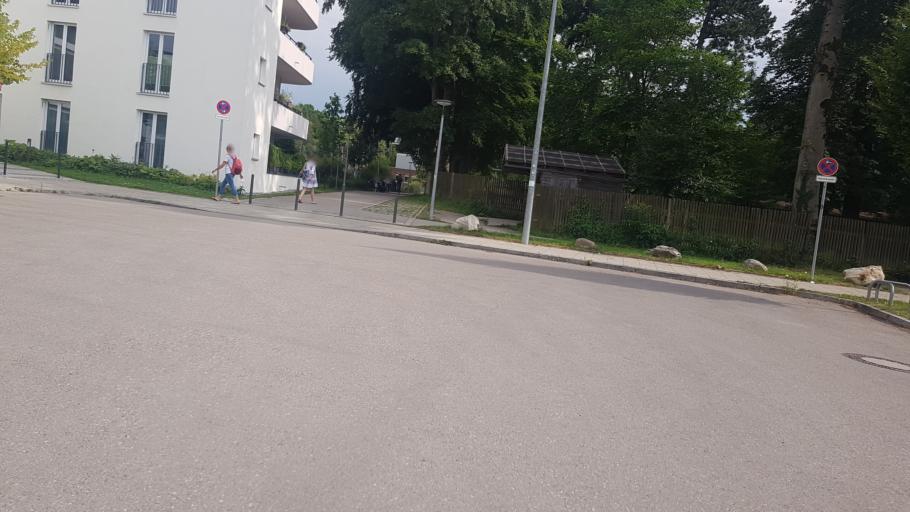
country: DE
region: Bavaria
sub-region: Upper Bavaria
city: Pullach im Isartal
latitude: 48.1055
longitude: 11.5352
